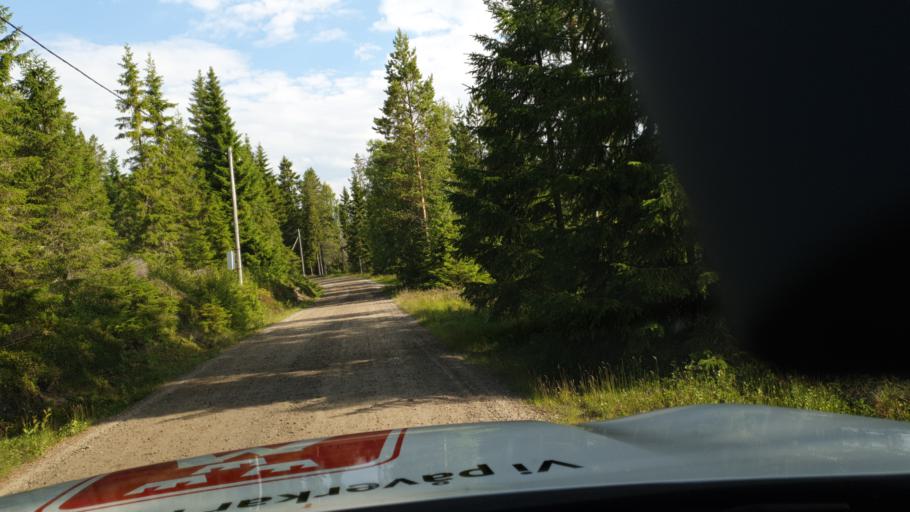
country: SE
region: Vaesterbotten
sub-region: Robertsfors Kommun
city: Robertsfors
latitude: 64.2145
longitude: 21.0777
